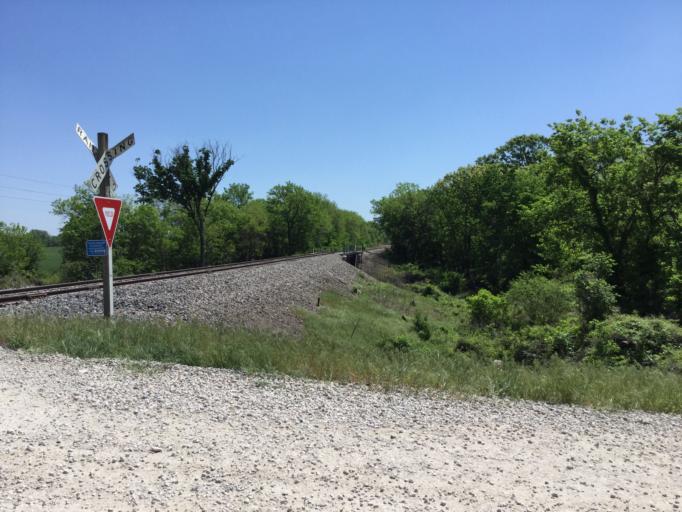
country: US
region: Kansas
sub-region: Montgomery County
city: Independence
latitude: 37.2106
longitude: -95.6930
